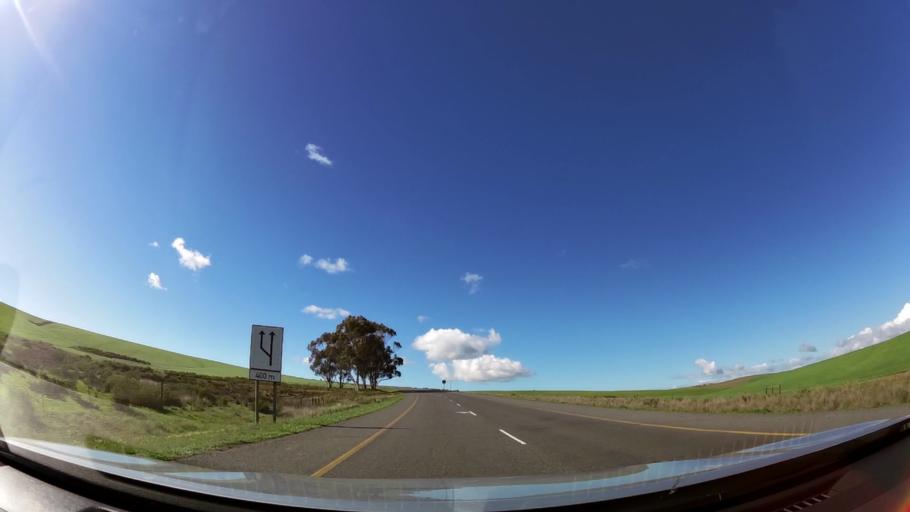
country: ZA
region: Western Cape
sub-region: Overberg District Municipality
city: Caledon
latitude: -34.1852
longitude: 19.6992
